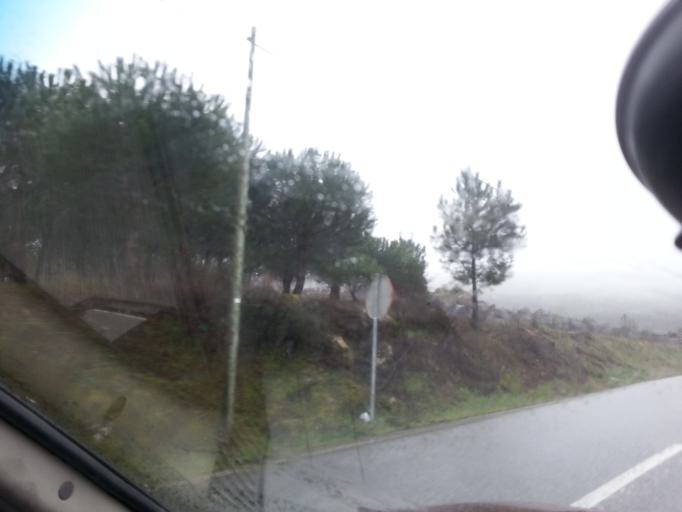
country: PT
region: Viseu
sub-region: Mangualde
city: Mangualde
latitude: 40.6097
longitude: -7.7025
